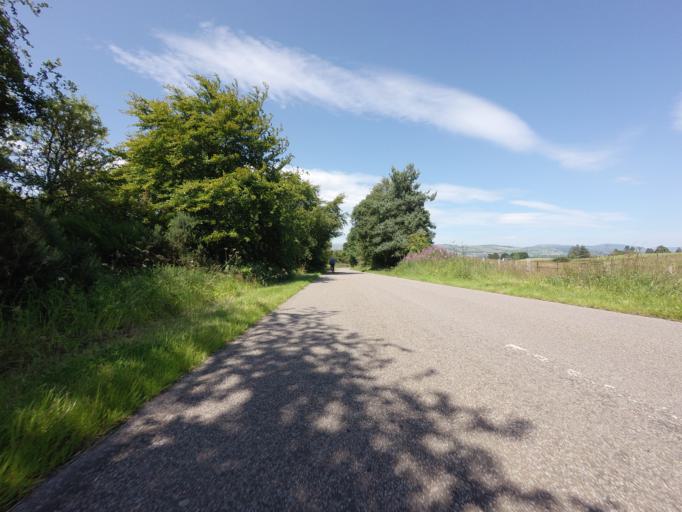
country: GB
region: Scotland
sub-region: Highland
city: Conon Bridge
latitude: 57.5644
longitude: -4.4215
